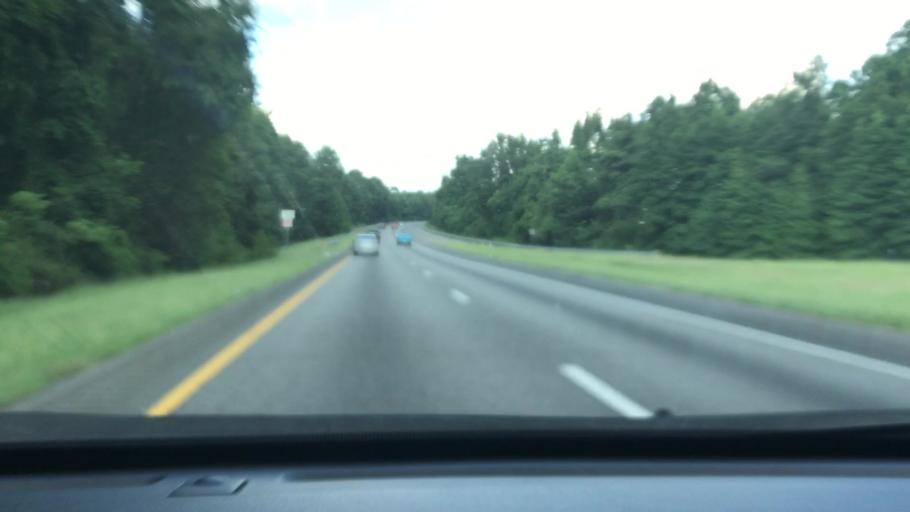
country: US
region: South Carolina
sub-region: Florence County
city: Florence
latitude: 34.2800
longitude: -79.6843
